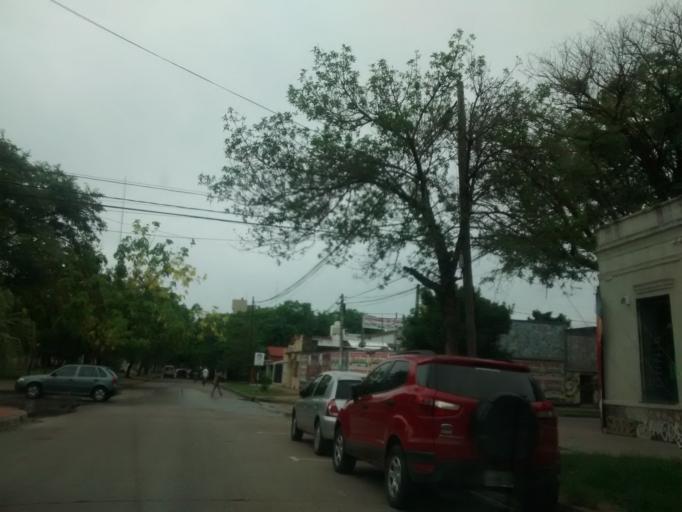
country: AR
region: Chaco
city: Resistencia
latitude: -27.4502
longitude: -58.9807
